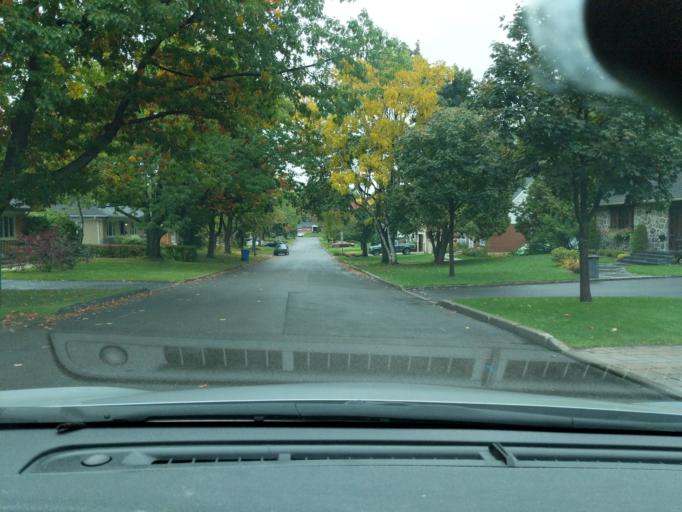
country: CA
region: Quebec
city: Quebec
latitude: 46.7652
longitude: -71.2732
